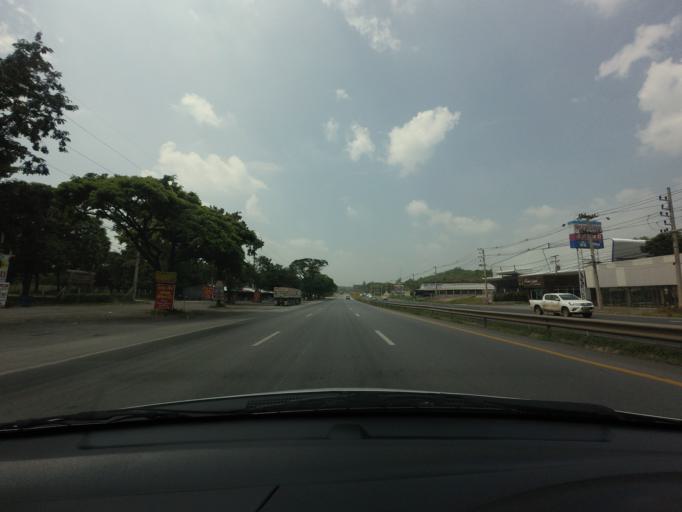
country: TH
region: Nakhon Ratchasima
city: Pak Chong
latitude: 14.6581
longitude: 101.3783
